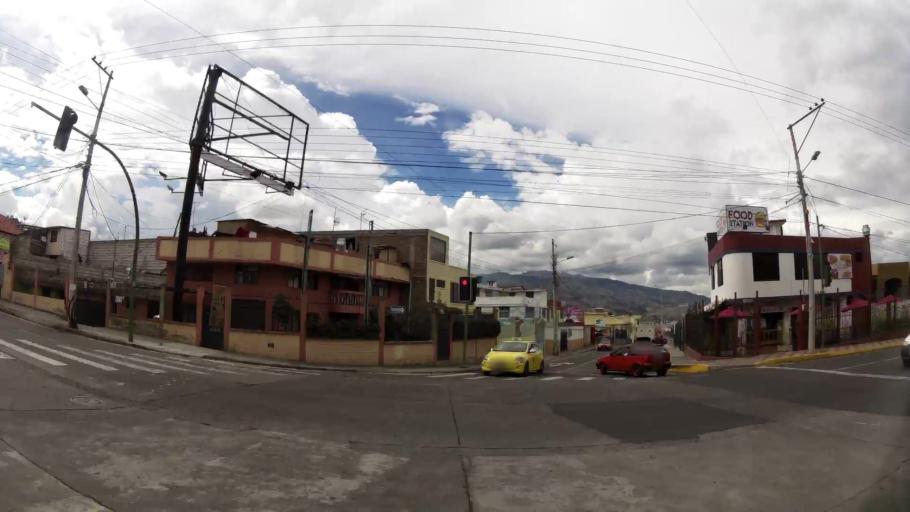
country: EC
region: Tungurahua
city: Ambato
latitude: -1.2646
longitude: -78.6289
